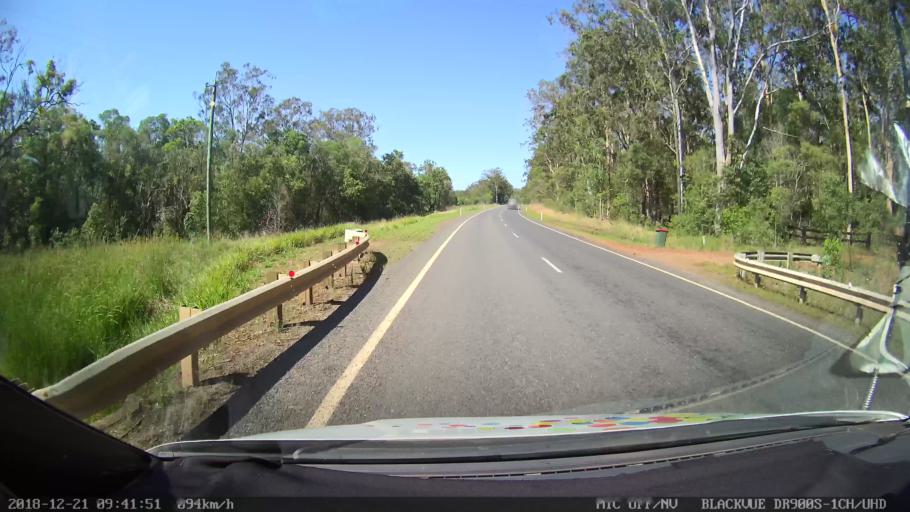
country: AU
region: New South Wales
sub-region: Clarence Valley
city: Grafton
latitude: -29.5898
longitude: 152.9530
